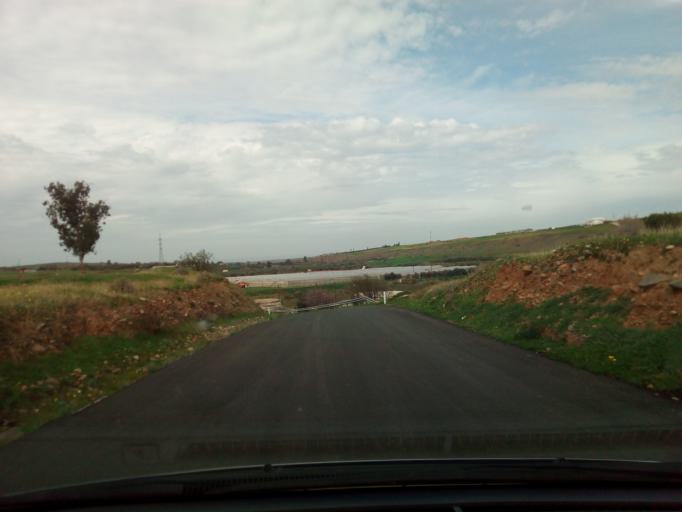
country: CY
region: Lefkosia
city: Astromeritis
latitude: 35.0941
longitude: 32.9919
